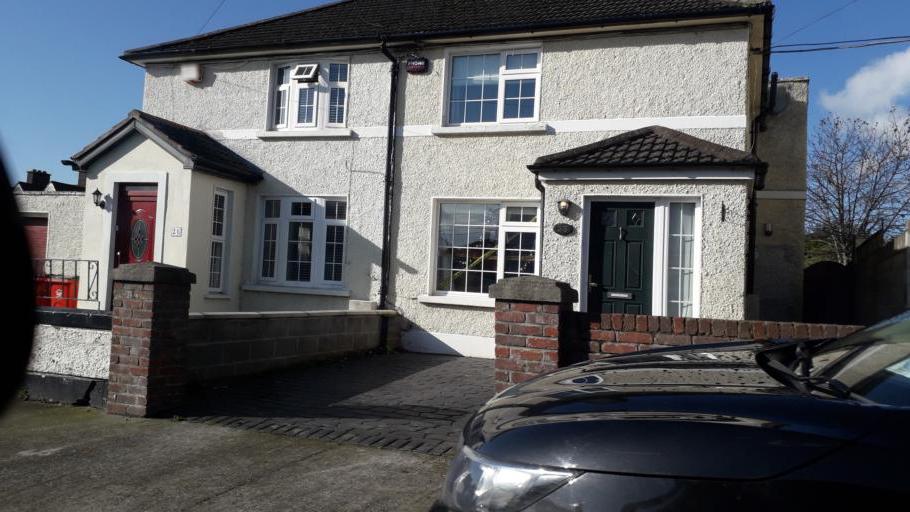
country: IE
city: Donnycarney
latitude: 53.3756
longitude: -6.2158
